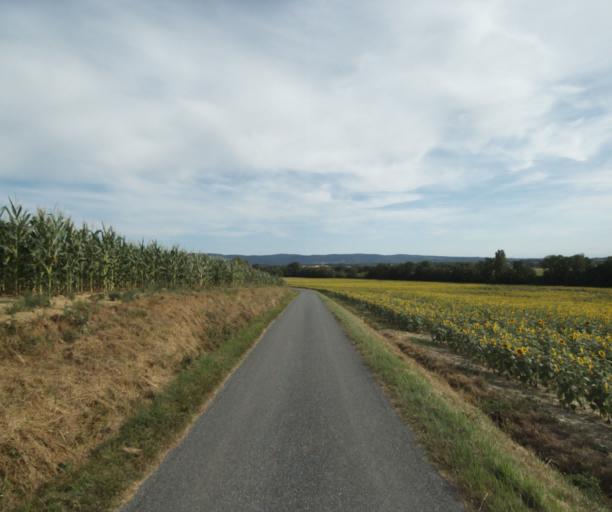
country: FR
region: Midi-Pyrenees
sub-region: Departement du Tarn
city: Puylaurens
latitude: 43.5332
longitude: 2.0445
